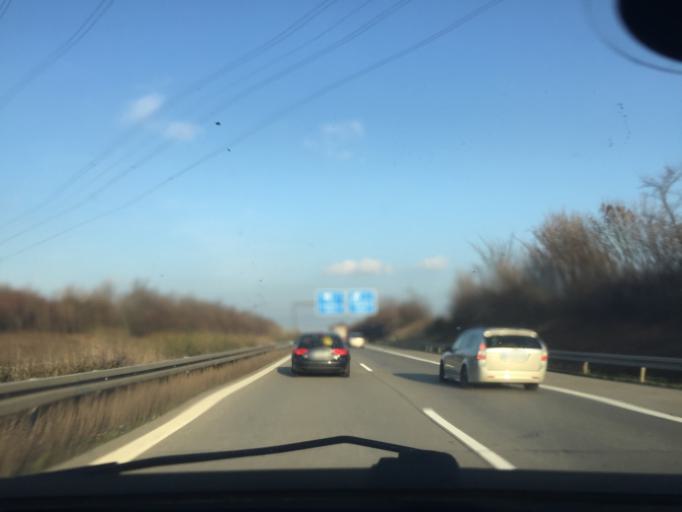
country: DE
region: Saxony-Anhalt
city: Diesdorf
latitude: 52.1336
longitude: 11.5361
